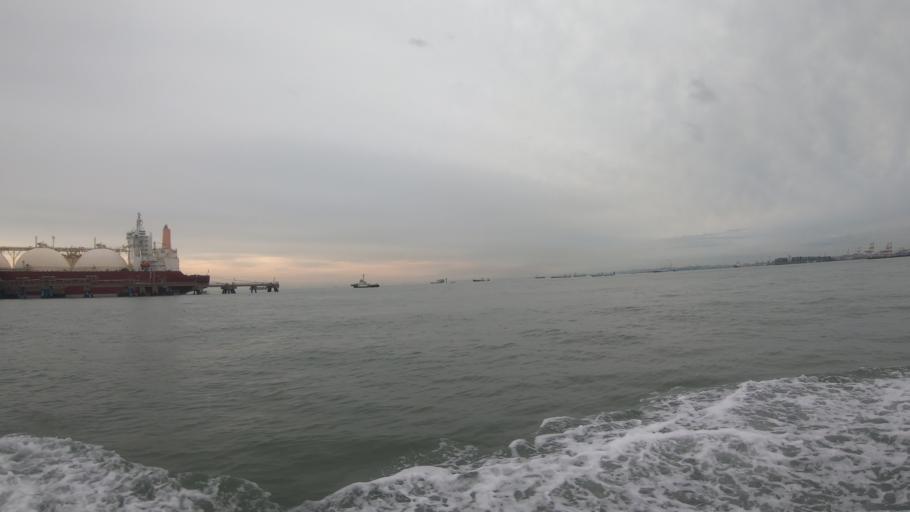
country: JP
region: Kanagawa
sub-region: Kawasaki-shi
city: Kawasaki
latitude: 35.4633
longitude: 139.7153
